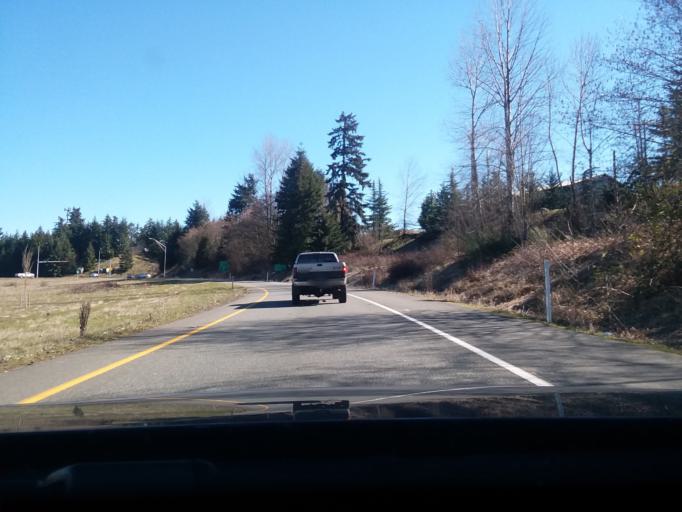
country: US
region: Washington
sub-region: Pierce County
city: Puyallup
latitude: 47.1597
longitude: -122.2982
